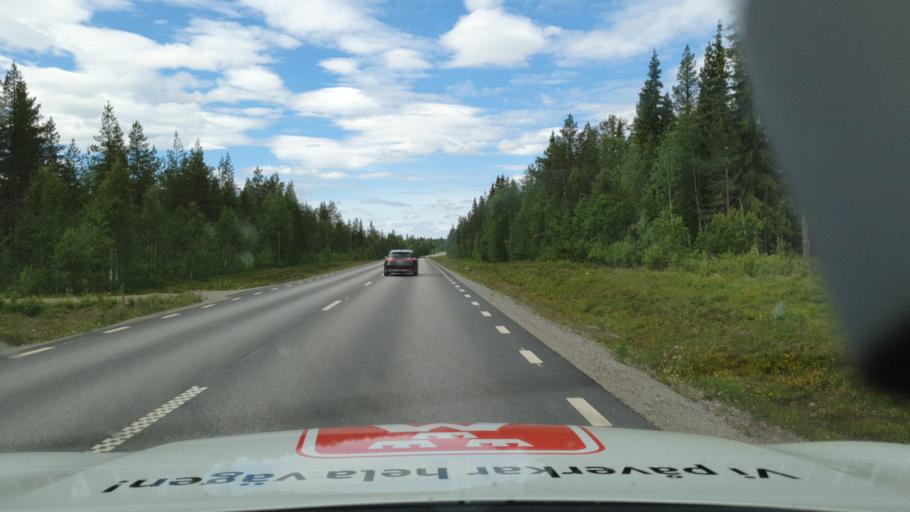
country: SE
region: Vaesterbotten
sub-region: Norsjo Kommun
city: Norsjoe
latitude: 65.2181
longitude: 19.7696
